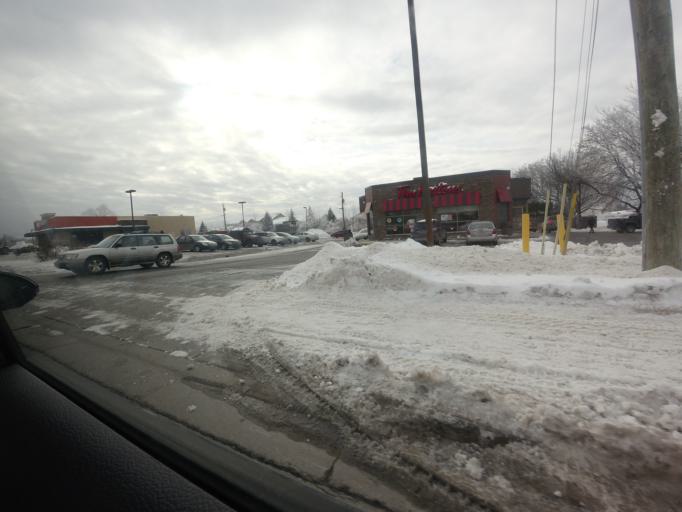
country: CA
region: New Brunswick
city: Fredericton
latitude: 45.9696
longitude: -66.6324
